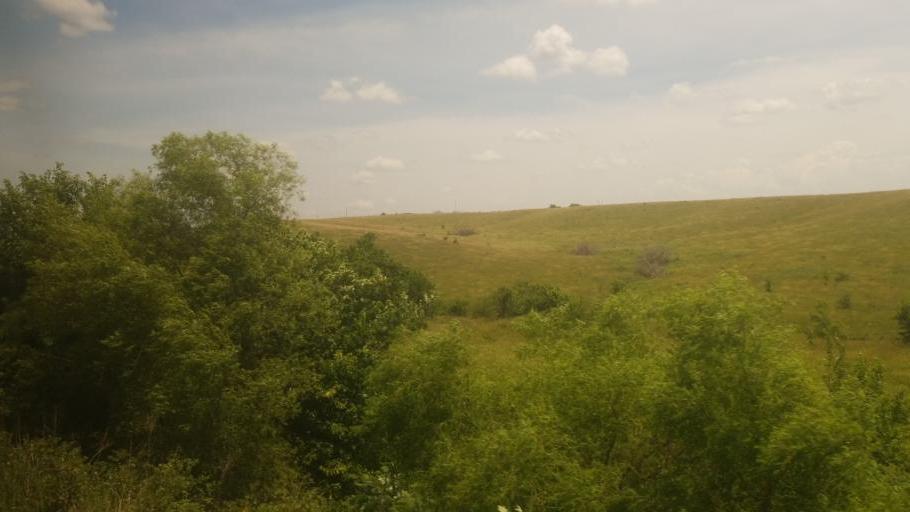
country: US
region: Missouri
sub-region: Linn County
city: Marceline
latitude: 39.8526
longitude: -92.8107
